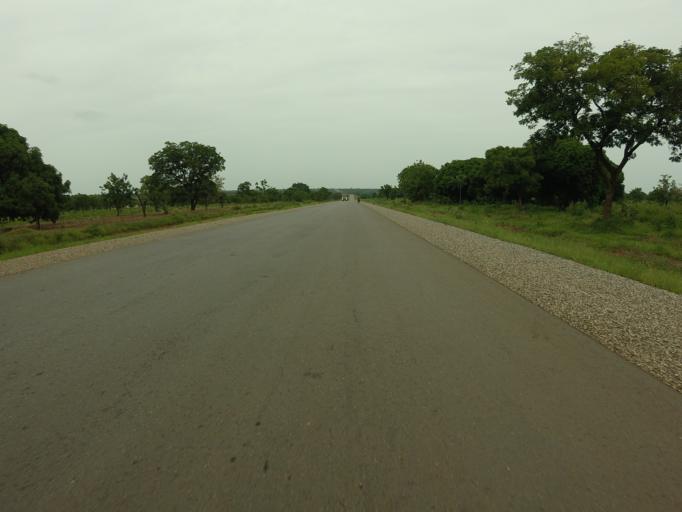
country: GH
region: Northern
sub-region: Yendi
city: Yendi
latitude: 9.2719
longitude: 0.0181
